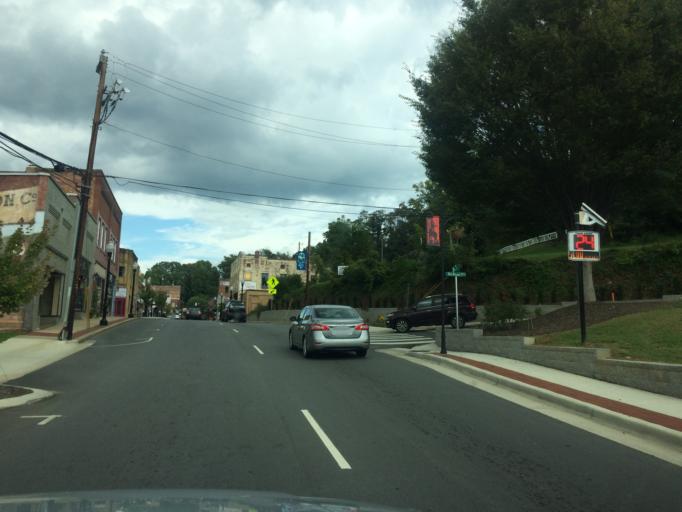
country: US
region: North Carolina
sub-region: Haywood County
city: Canton
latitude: 35.5312
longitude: -82.8405
